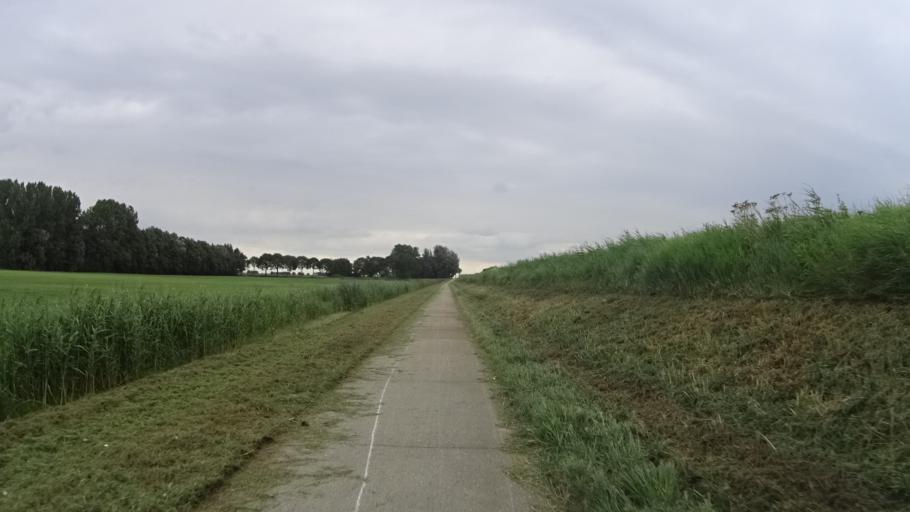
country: NL
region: Groningen
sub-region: Gemeente Groningen
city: Oosterpark
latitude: 53.2357
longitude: 6.6571
